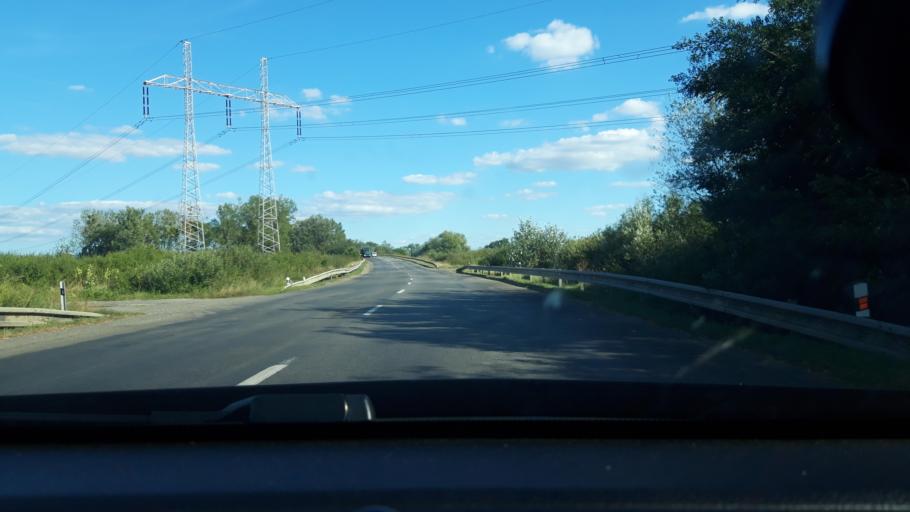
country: SK
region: Kosicky
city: Cierna nad Tisou
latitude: 48.5610
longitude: 21.9957
